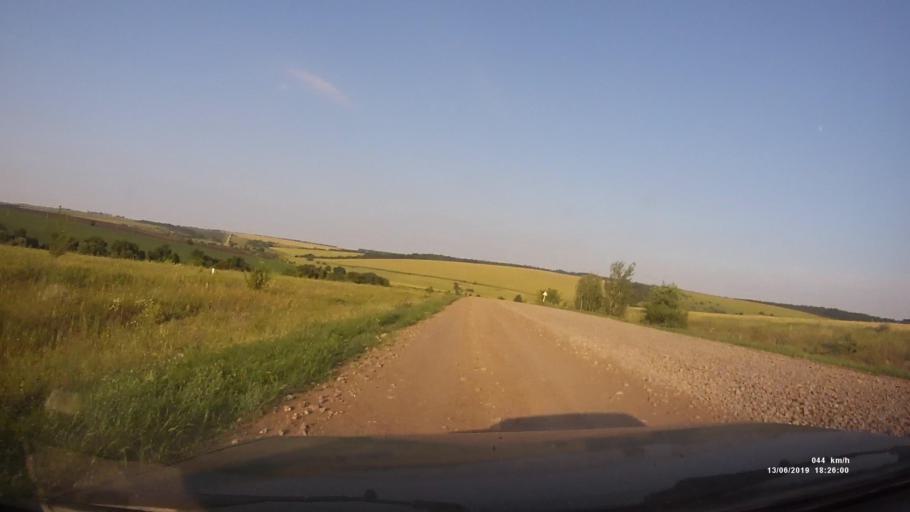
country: RU
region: Rostov
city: Kazanskaya
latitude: 49.8511
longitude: 41.3079
